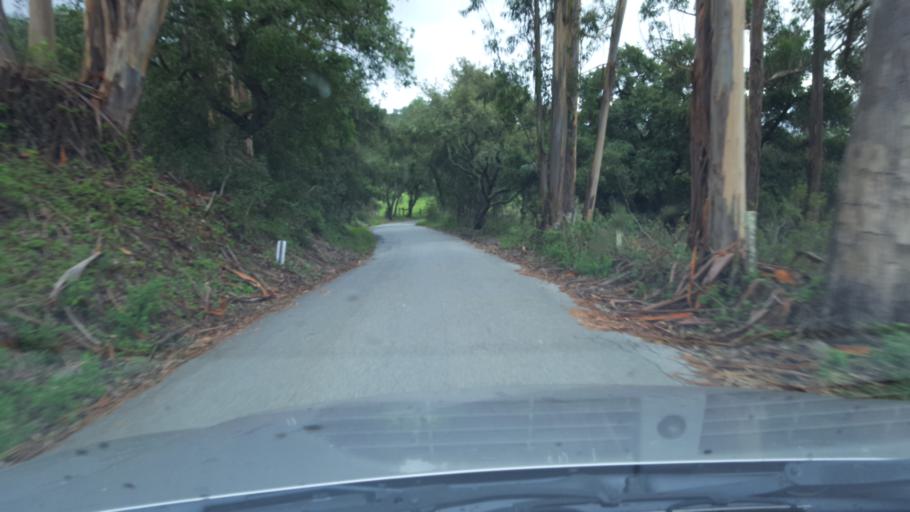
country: US
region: California
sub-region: Santa Cruz County
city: Interlaken
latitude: 36.9978
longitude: -121.7305
